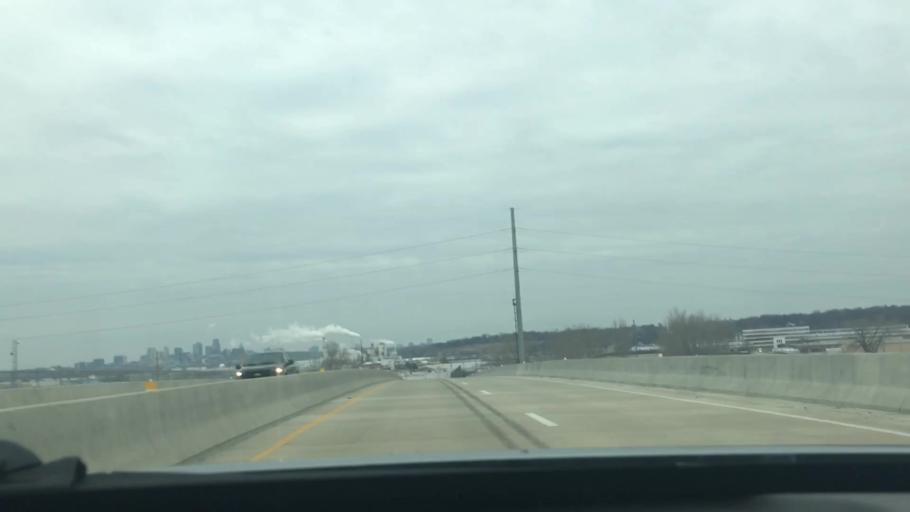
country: US
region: Missouri
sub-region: Platte County
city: Riverside
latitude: 39.1557
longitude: -94.6233
